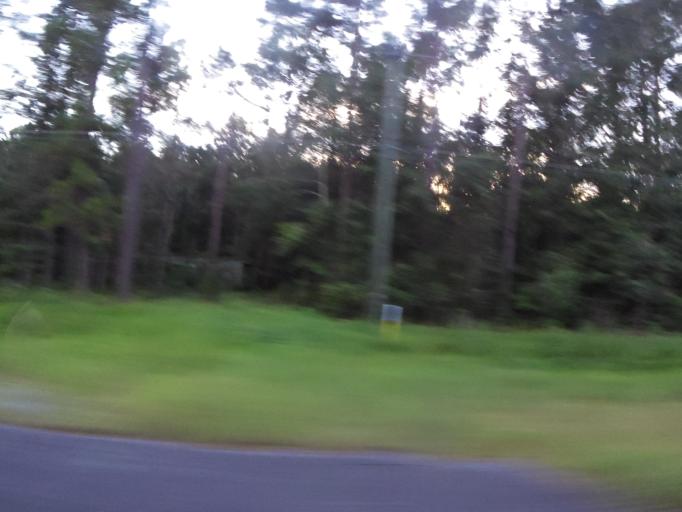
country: US
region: Georgia
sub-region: Camden County
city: Woodbine
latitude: 30.9161
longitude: -81.7131
